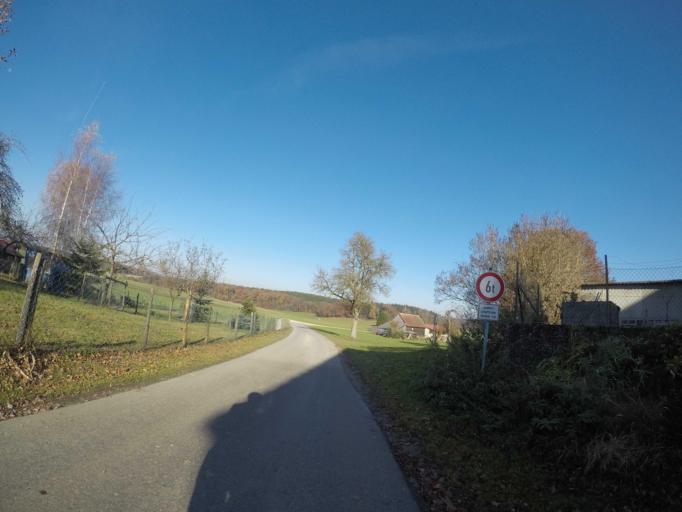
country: DE
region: Baden-Wuerttemberg
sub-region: Tuebingen Region
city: Obermarchtal
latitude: 48.2086
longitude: 9.5645
